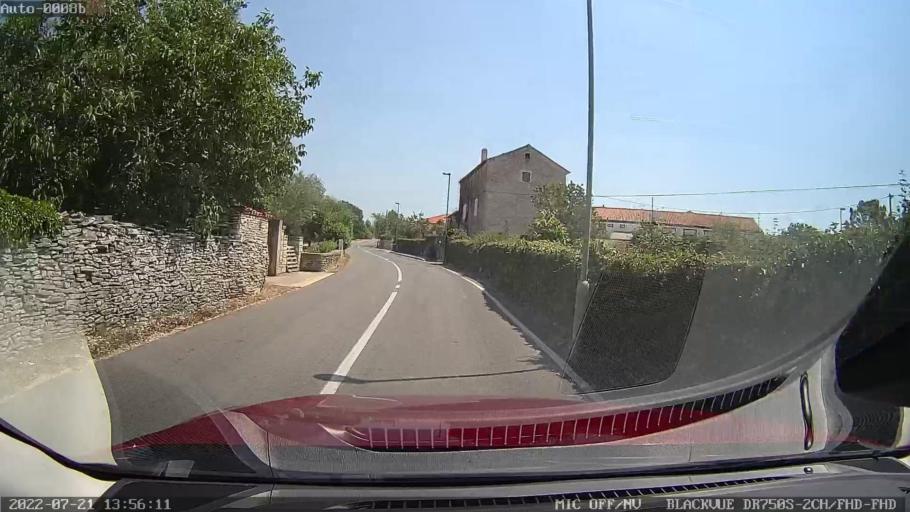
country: HR
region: Istarska
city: Pazin
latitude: 45.1206
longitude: 13.8404
